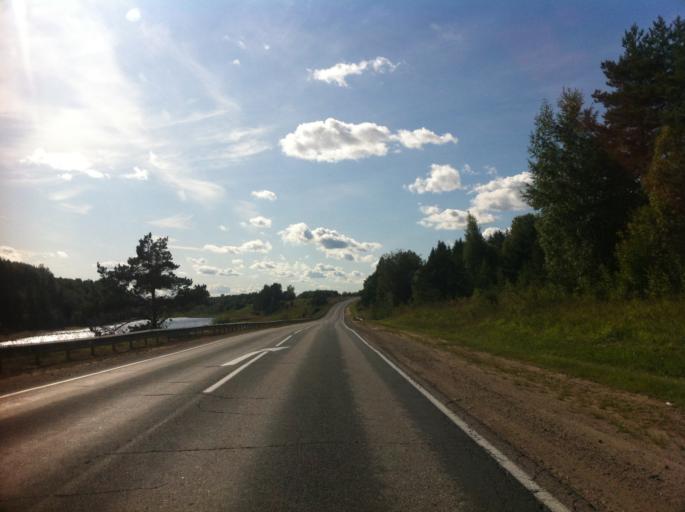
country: RU
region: Pskov
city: Izborsk
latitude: 57.7493
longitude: 27.7434
